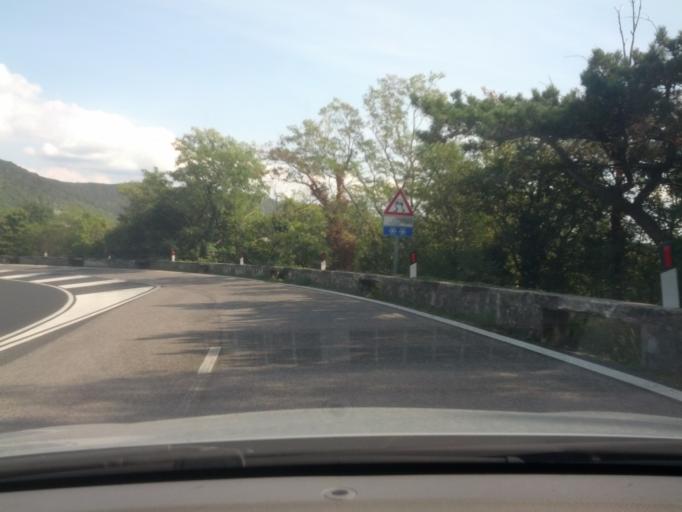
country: IT
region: Friuli Venezia Giulia
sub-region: Provincia di Trieste
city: Villa Opicina
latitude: 45.6672
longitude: 13.7908
